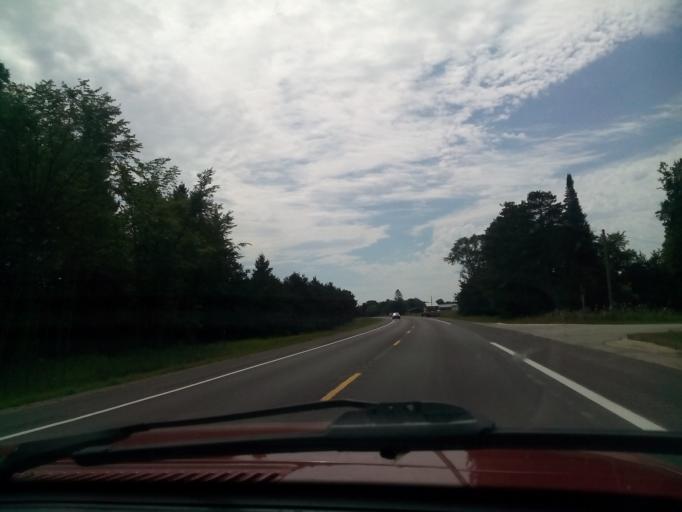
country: US
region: Michigan
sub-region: Schoolcraft County
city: Manistique
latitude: 46.0811
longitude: -85.9576
